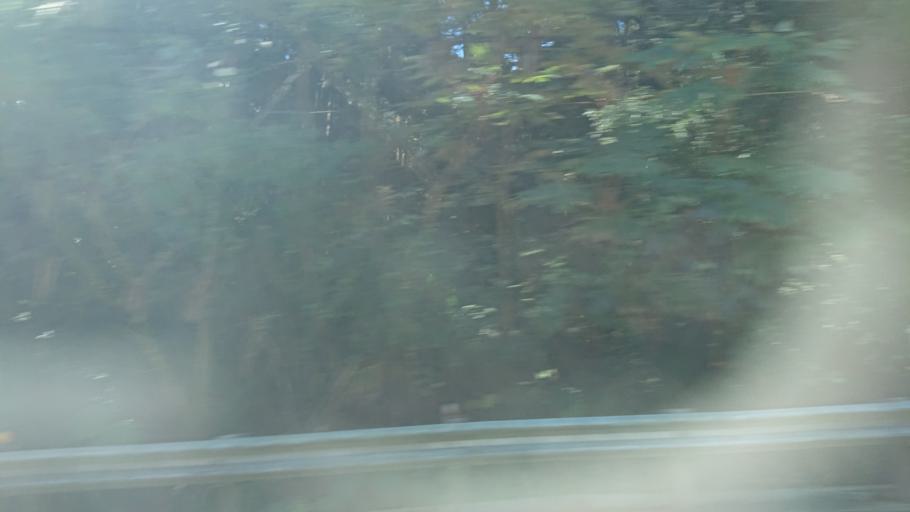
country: TW
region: Taiwan
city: Lugu
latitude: 23.4954
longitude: 120.7791
